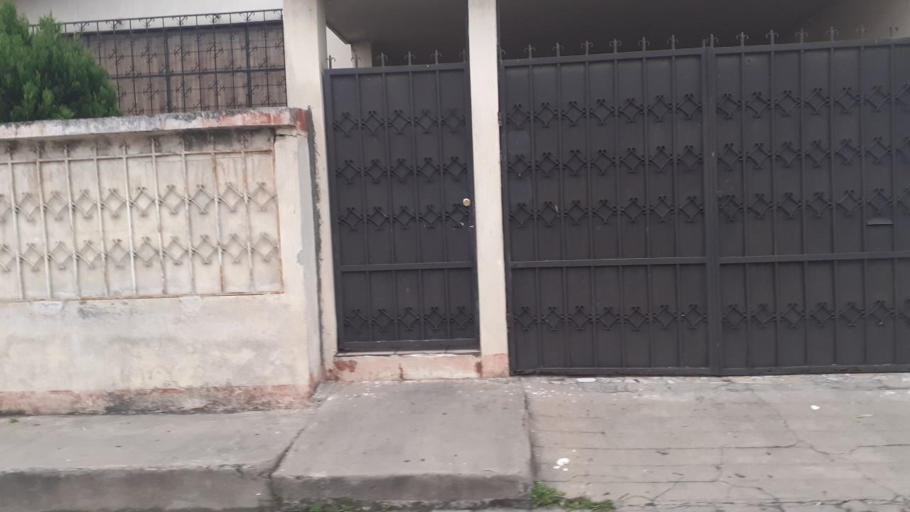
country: GT
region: Quetzaltenango
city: Quetzaltenango
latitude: 14.8402
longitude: -91.5283
